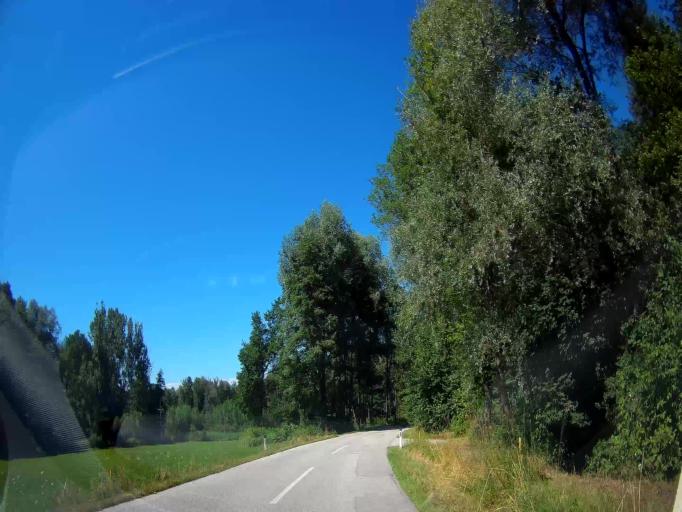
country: AT
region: Carinthia
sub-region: Politischer Bezirk Klagenfurt Land
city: Grafenstein
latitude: 46.6006
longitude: 14.4394
